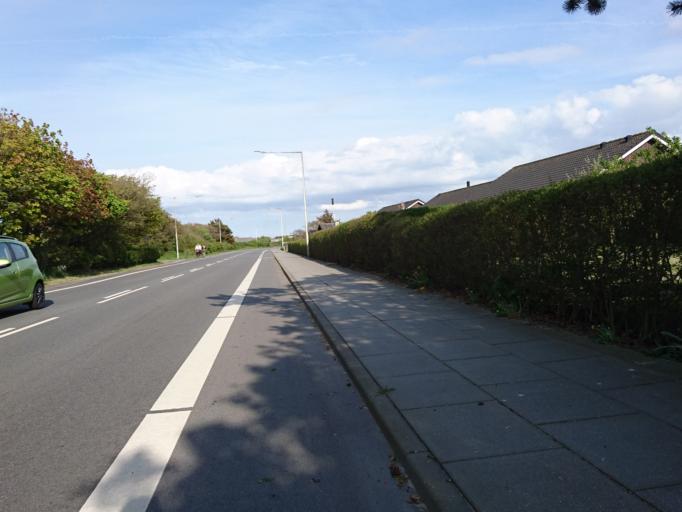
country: DK
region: North Denmark
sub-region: Frederikshavn Kommune
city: Skagen
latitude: 57.7293
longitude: 10.5523
